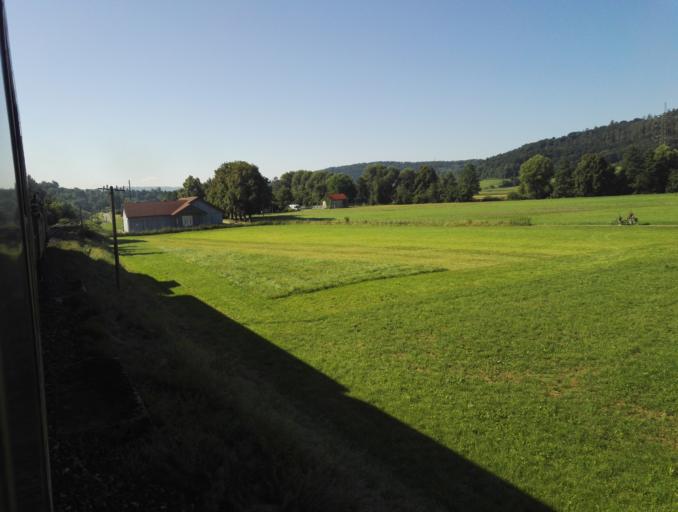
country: DE
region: Baden-Wuerttemberg
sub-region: Regierungsbezirk Stuttgart
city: Rudersberg
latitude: 48.8599
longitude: 9.5369
